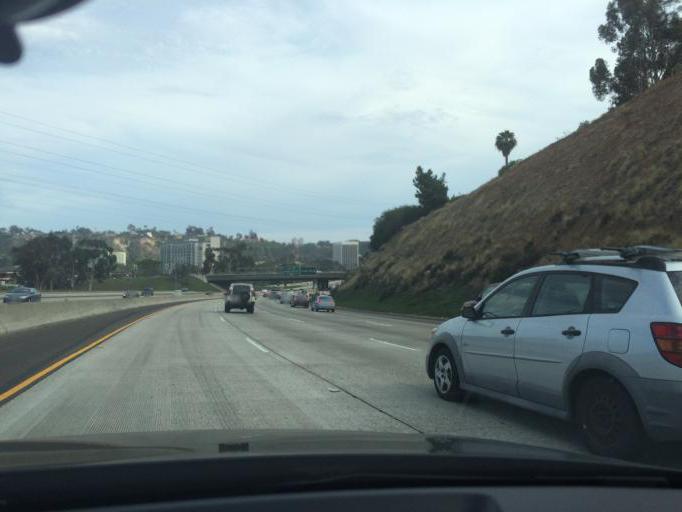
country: US
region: California
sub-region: San Diego County
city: San Diego
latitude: 32.7749
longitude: -117.1614
